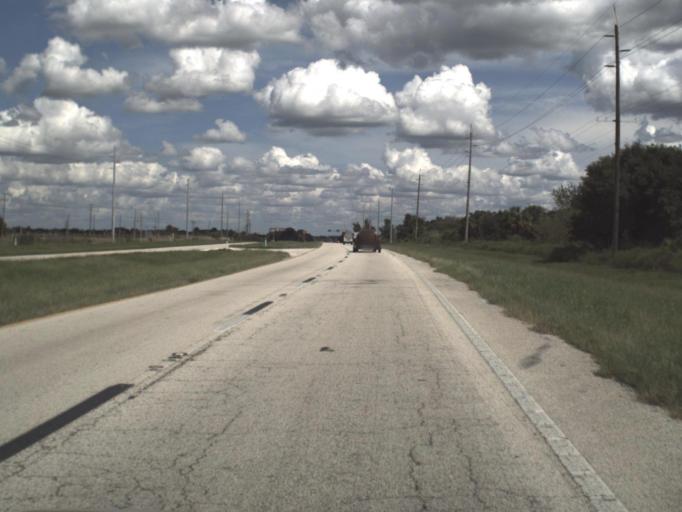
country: US
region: Florida
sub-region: Polk County
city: Bartow
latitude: 27.8979
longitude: -81.8845
